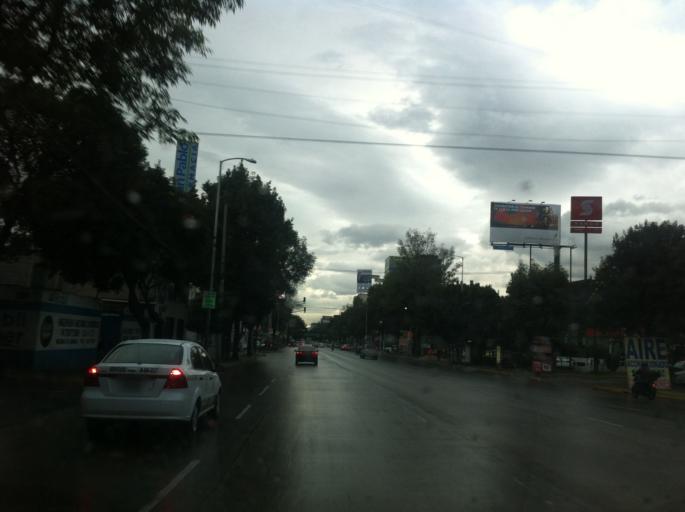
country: MX
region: Mexico City
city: Colonia del Valle
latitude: 19.3866
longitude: -99.1827
